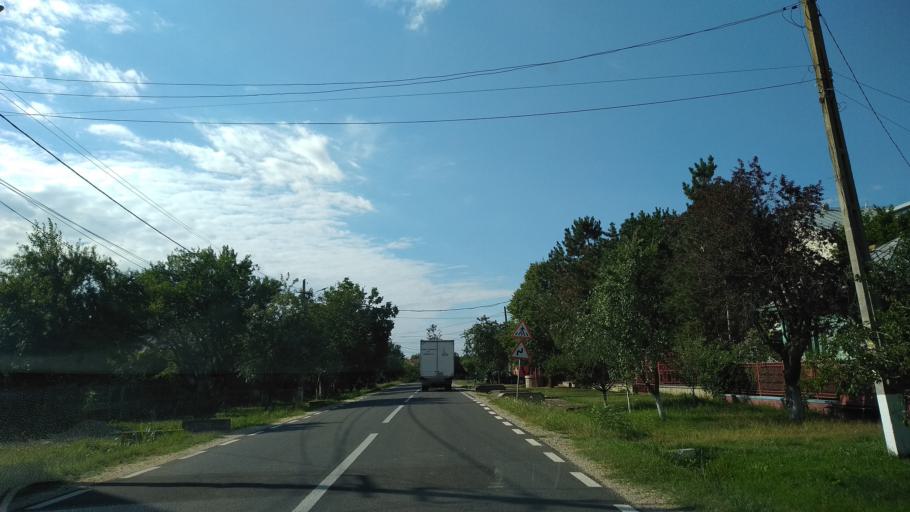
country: RO
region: Dambovita
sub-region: Comuna Uliesti
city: Uliesti
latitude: 44.6020
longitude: 25.3930
